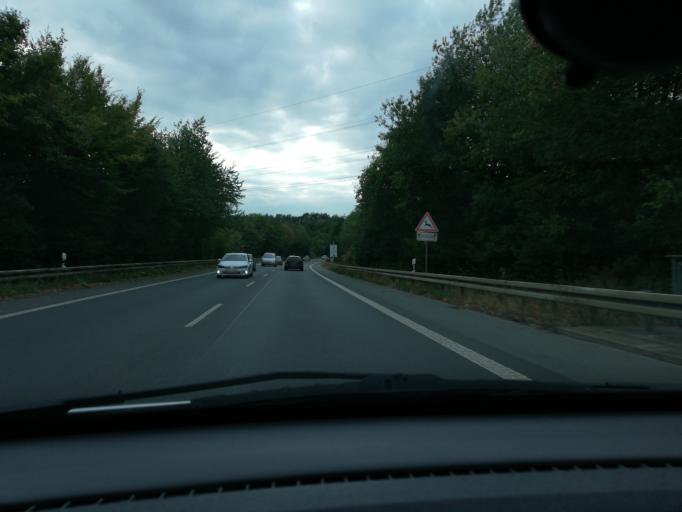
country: DE
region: North Rhine-Westphalia
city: Gevelsberg
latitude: 51.3320
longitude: 7.3654
